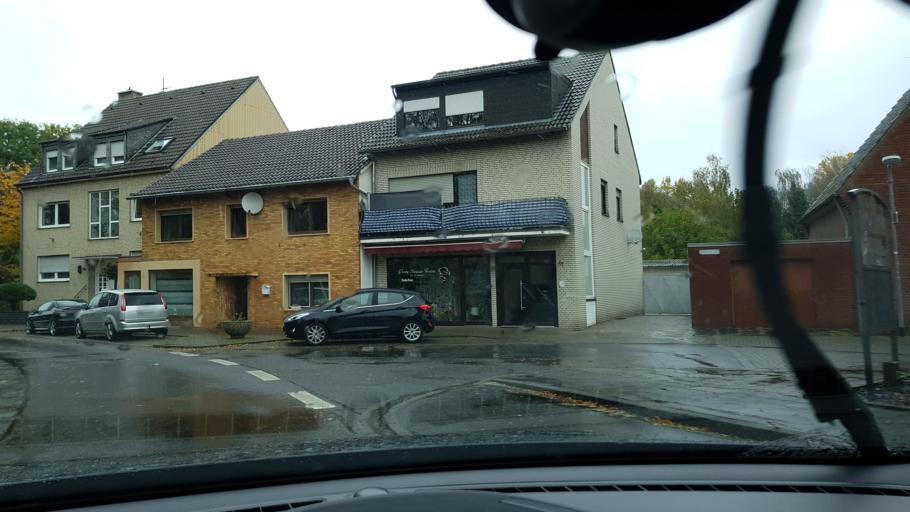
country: DE
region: North Rhine-Westphalia
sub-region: Regierungsbezirk Dusseldorf
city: Rommerskirchen
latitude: 51.0618
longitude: 6.7151
